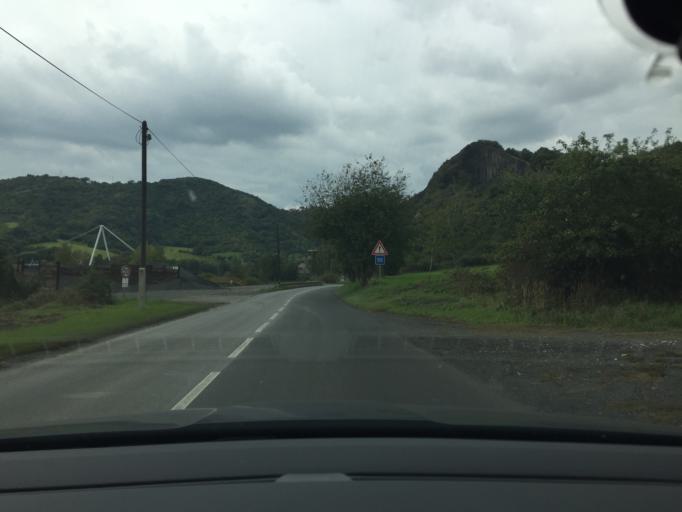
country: CZ
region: Ustecky
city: Lovosice
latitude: 50.5789
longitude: 14.0420
